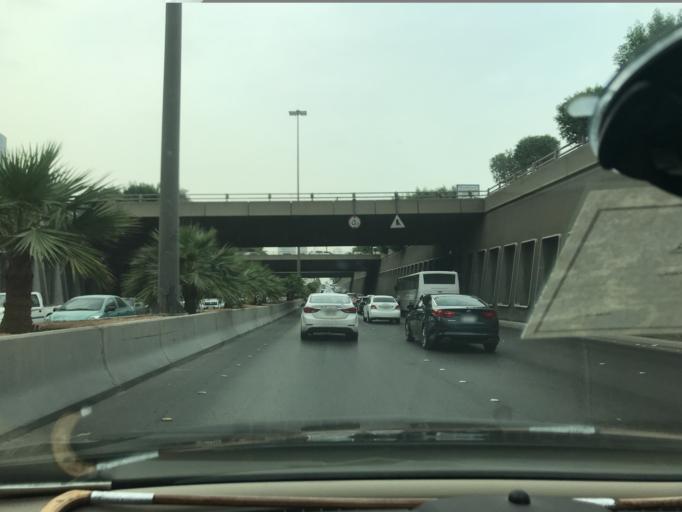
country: SA
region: Ar Riyad
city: Riyadh
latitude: 24.7108
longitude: 46.6723
